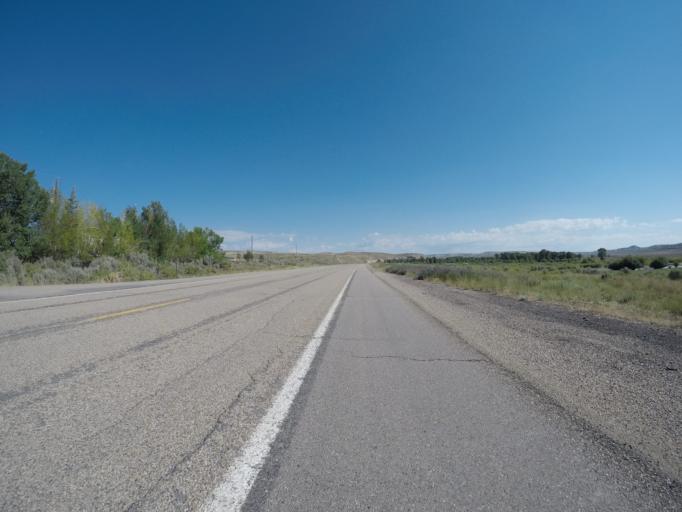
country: US
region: Wyoming
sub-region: Sublette County
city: Marbleton
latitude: 42.1633
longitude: -110.1886
